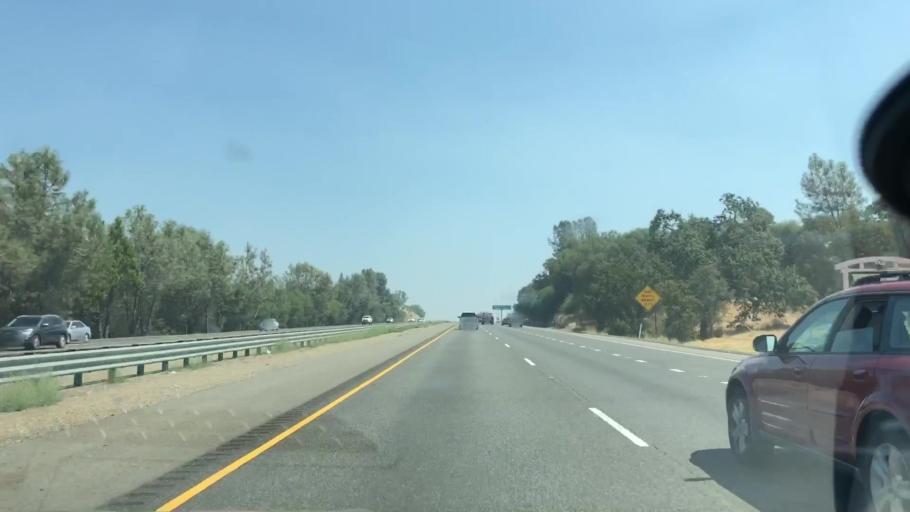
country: US
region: California
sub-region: El Dorado County
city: Shingle Springs
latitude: 38.6843
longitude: -120.9108
